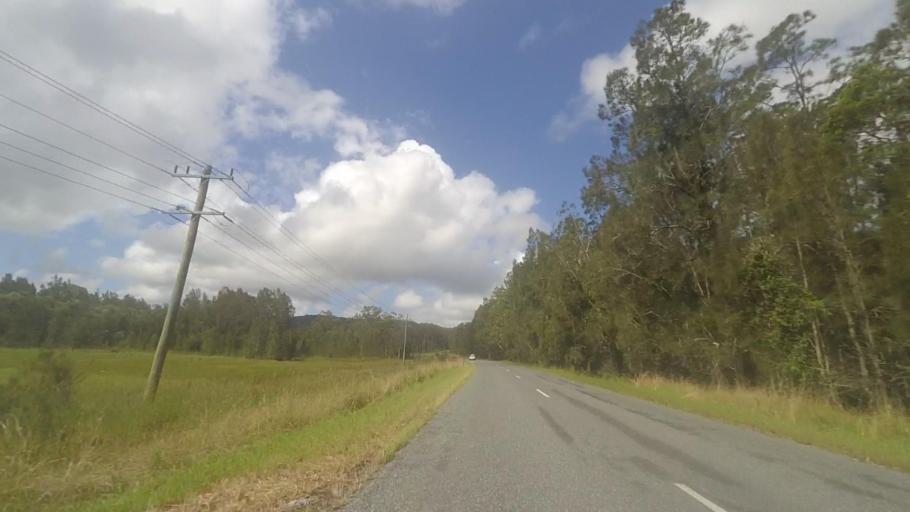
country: AU
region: New South Wales
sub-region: Great Lakes
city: Bulahdelah
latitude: -32.3846
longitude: 152.3407
